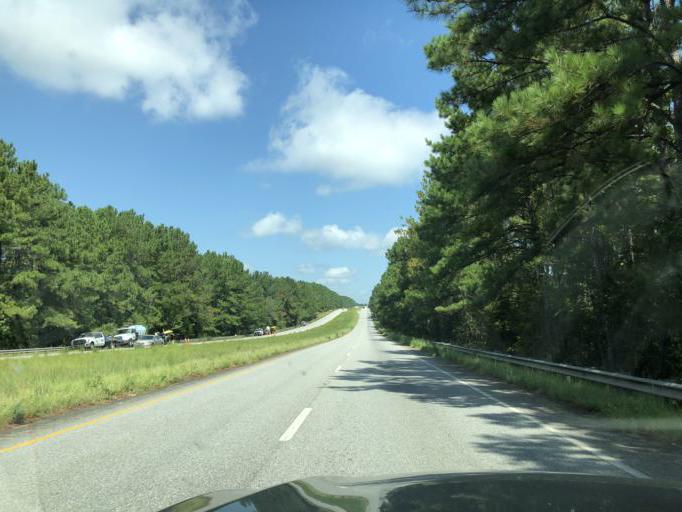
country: US
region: Alabama
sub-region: Henry County
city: Abbeville
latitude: 31.6716
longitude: -85.2795
